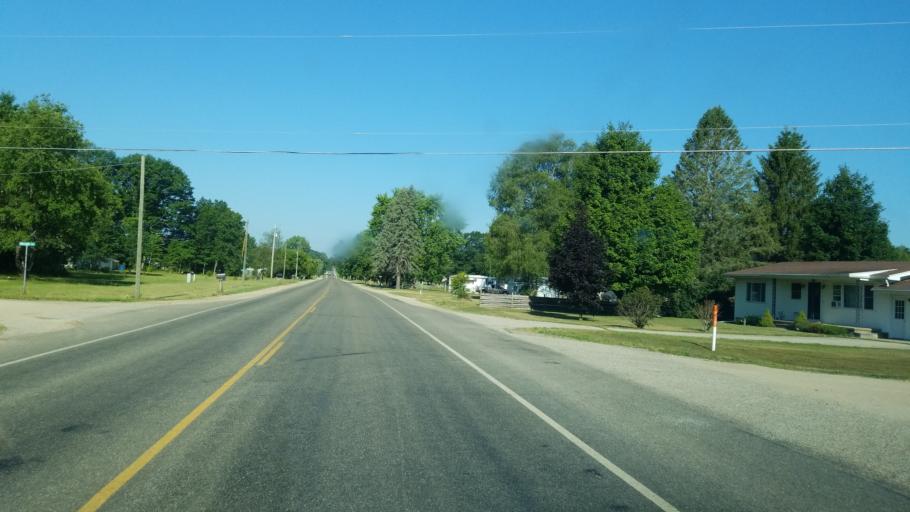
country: US
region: Michigan
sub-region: Montcalm County
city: Howard City
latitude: 43.4899
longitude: -85.4552
